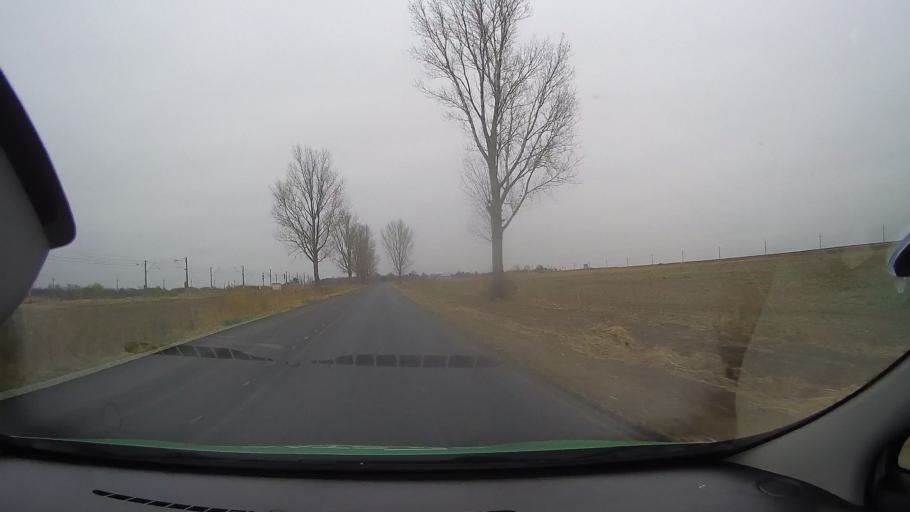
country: RO
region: Ialomita
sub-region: Comuna Valea Ciorii
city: Valea Ciorii
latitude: 44.7353
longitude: 27.5795
